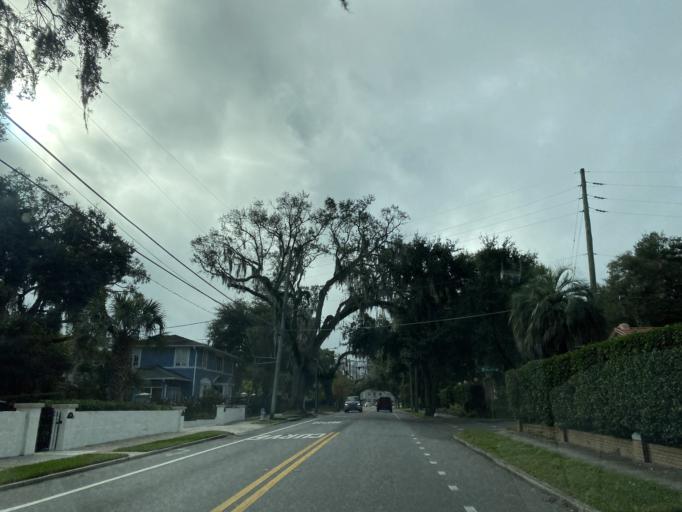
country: US
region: Florida
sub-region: Orange County
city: Orlando
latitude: 28.5550
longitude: -81.3877
